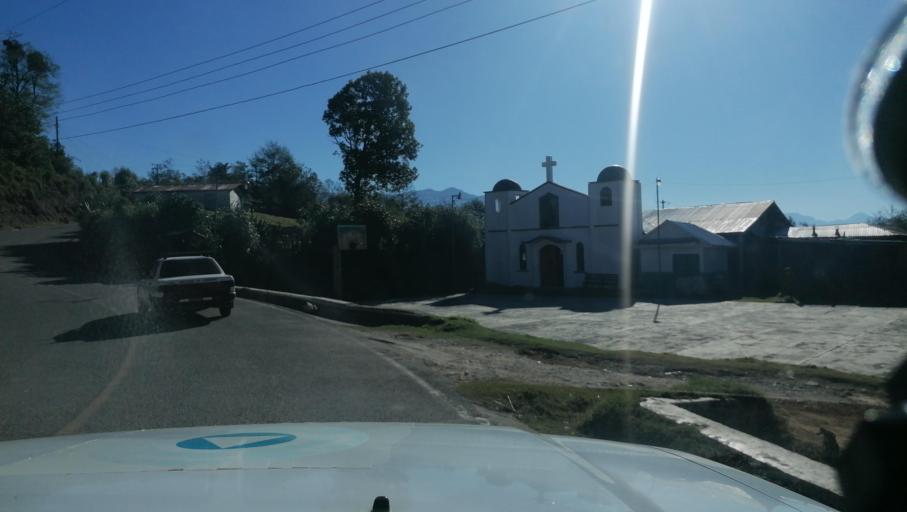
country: MX
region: Chiapas
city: Motozintla de Mendoza
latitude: 15.2477
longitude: -92.2272
